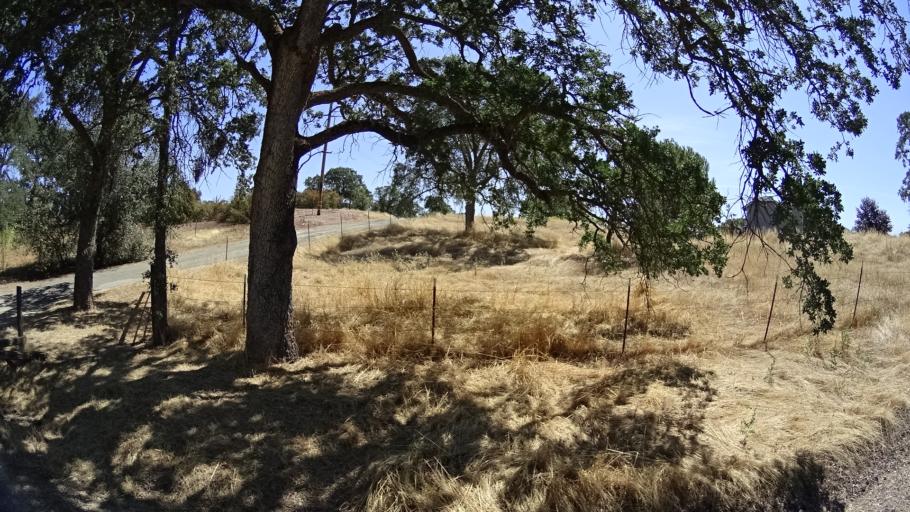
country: US
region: California
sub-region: Calaveras County
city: Rancho Calaveras
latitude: 38.1554
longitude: -120.9529
